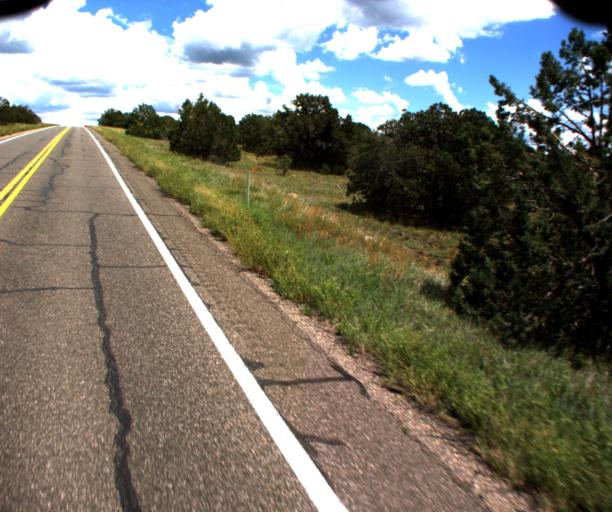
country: US
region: Arizona
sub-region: Gila County
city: Pine
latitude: 34.5146
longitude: -111.5363
